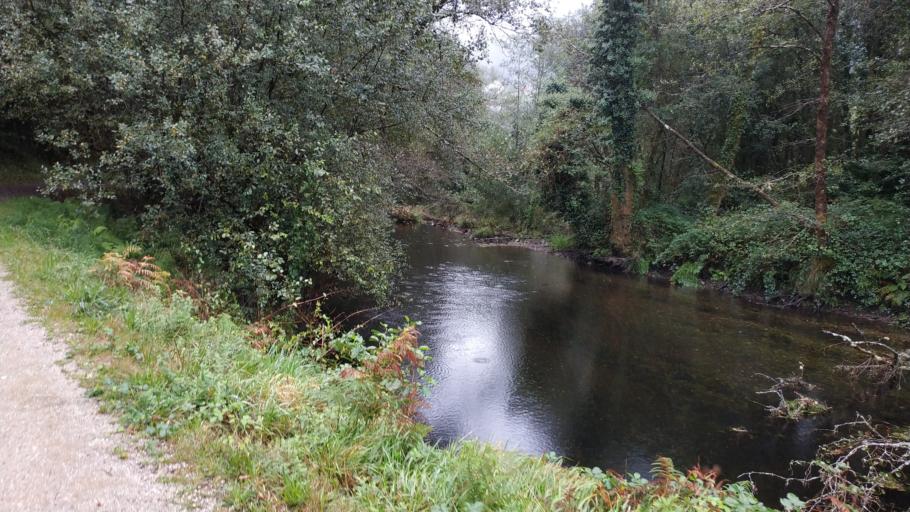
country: ES
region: Galicia
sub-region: Provincia da Coruna
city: Negreira
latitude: 42.9088
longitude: -8.7450
